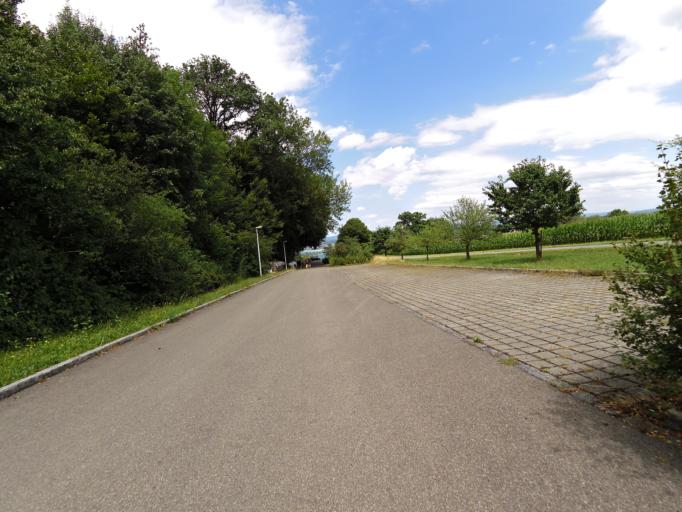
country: CH
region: Thurgau
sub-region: Kreuzlingen District
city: Ermatingen
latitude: 47.6550
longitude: 9.0800
